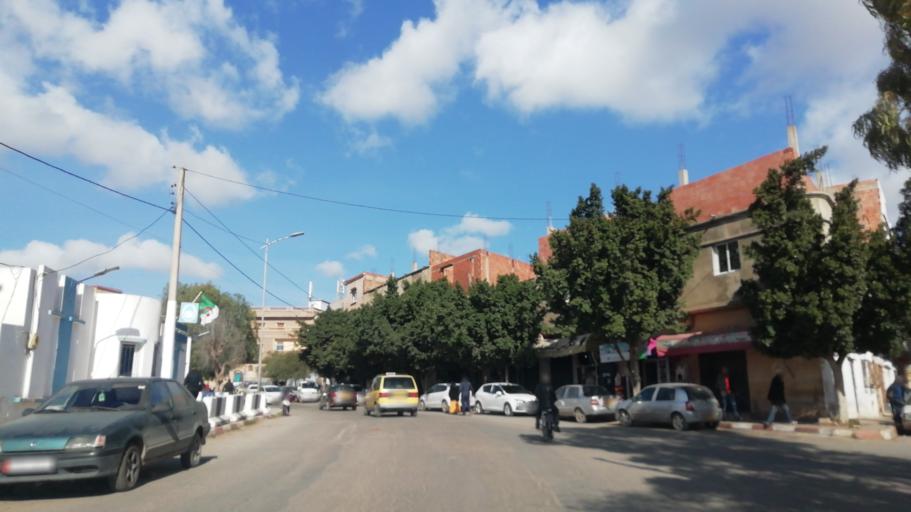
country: DZ
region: Oran
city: Es Senia
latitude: 35.6398
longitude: -0.6676
